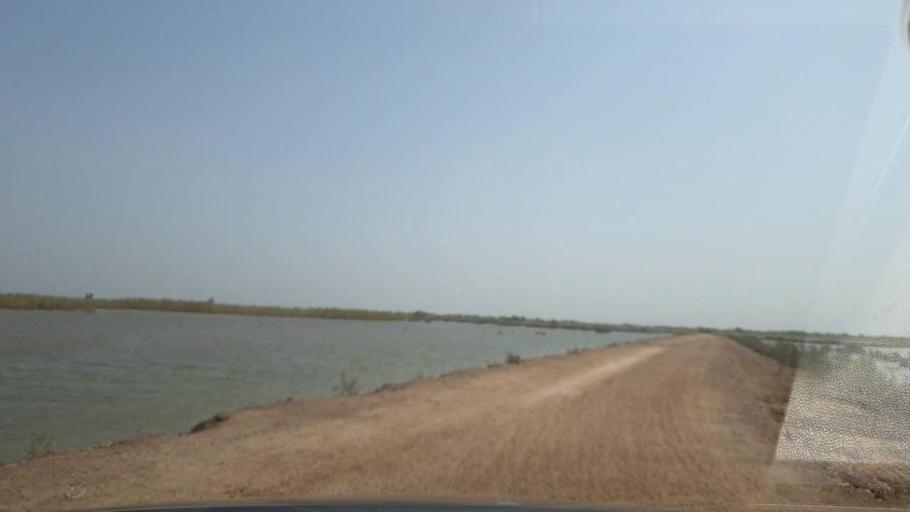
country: PK
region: Sindh
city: Tando Bago
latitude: 24.7920
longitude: 69.0788
